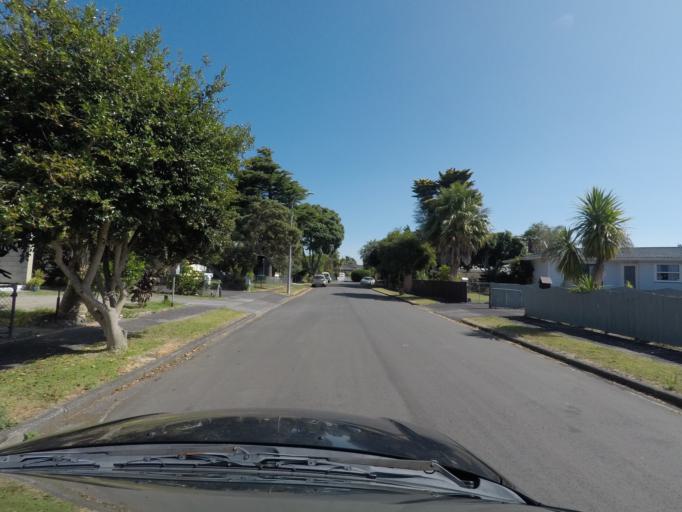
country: NZ
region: Auckland
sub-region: Auckland
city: Rosebank
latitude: -36.8863
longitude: 174.6803
